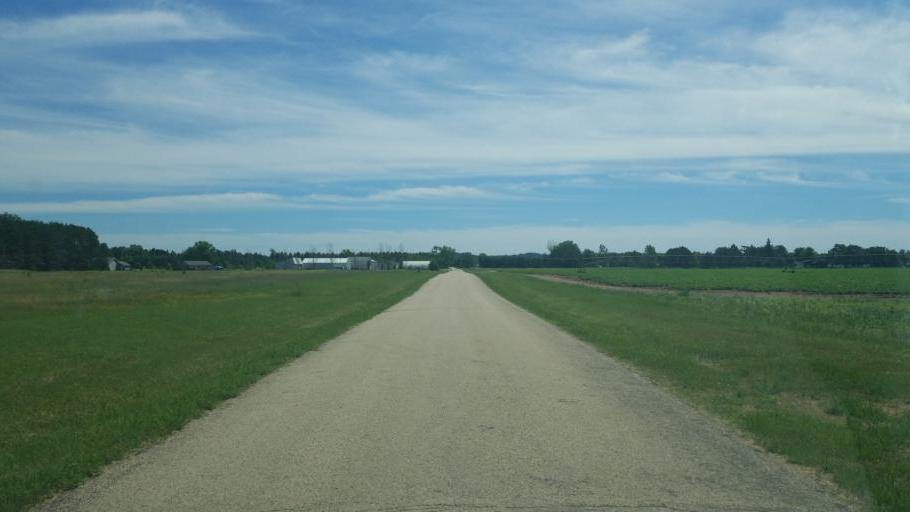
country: US
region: Wisconsin
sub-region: Adams County
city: Adams
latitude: 43.8764
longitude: -89.9448
